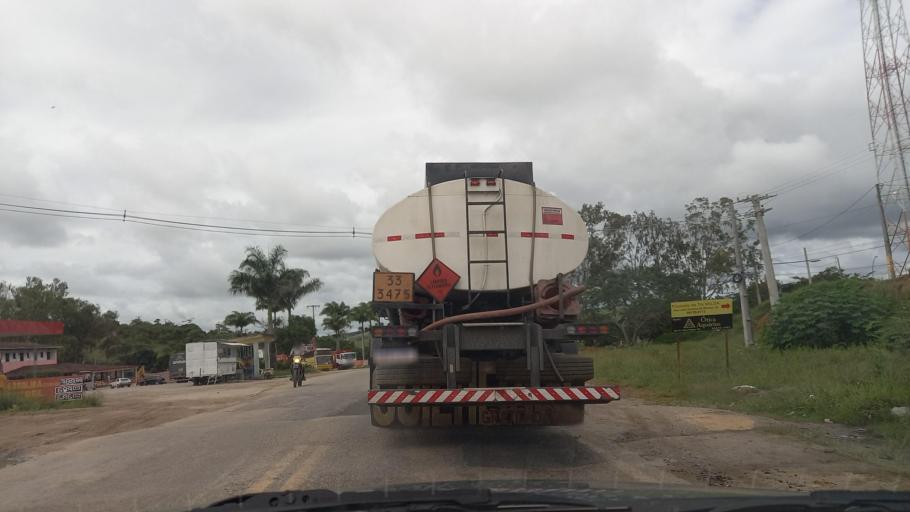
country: BR
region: Pernambuco
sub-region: Canhotinho
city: Canhotinho
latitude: -8.8732
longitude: -36.2015
